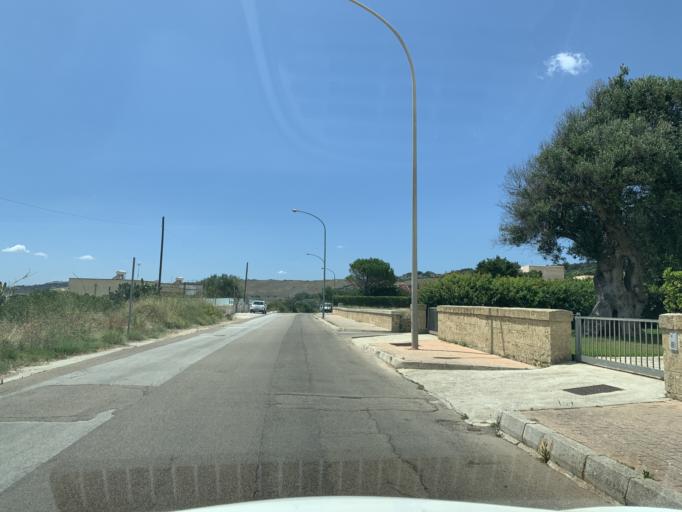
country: IT
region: Apulia
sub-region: Provincia di Lecce
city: Santa Cesarea Terme
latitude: 40.0333
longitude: 18.4515
